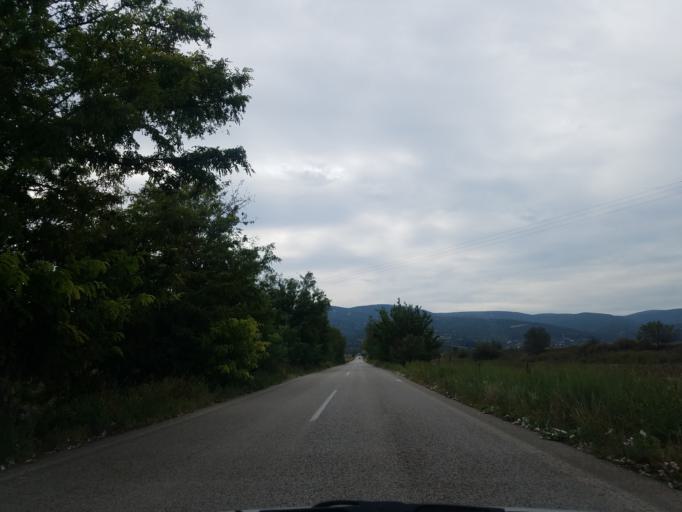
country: GR
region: Central Greece
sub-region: Nomos Fthiotidos
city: Domokos
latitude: 39.1656
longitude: 22.2944
